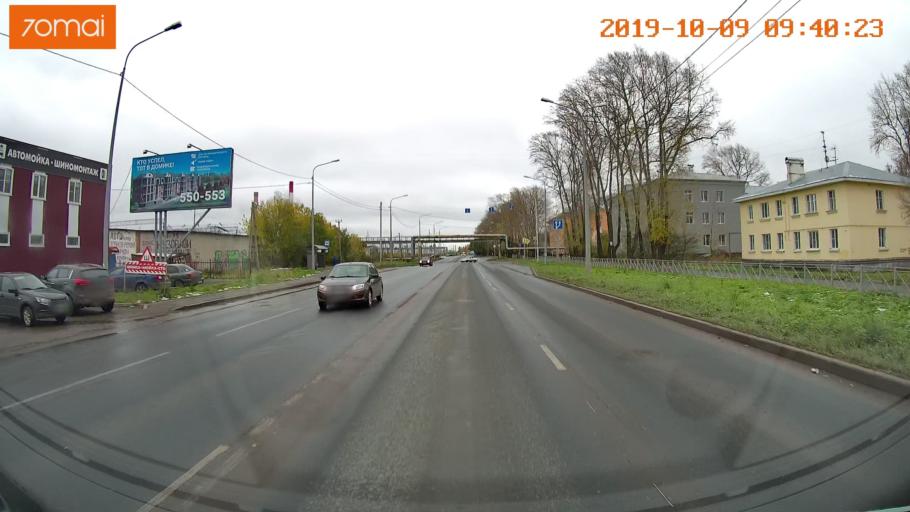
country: RU
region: Vologda
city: Vologda
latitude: 59.1953
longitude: 39.9253
